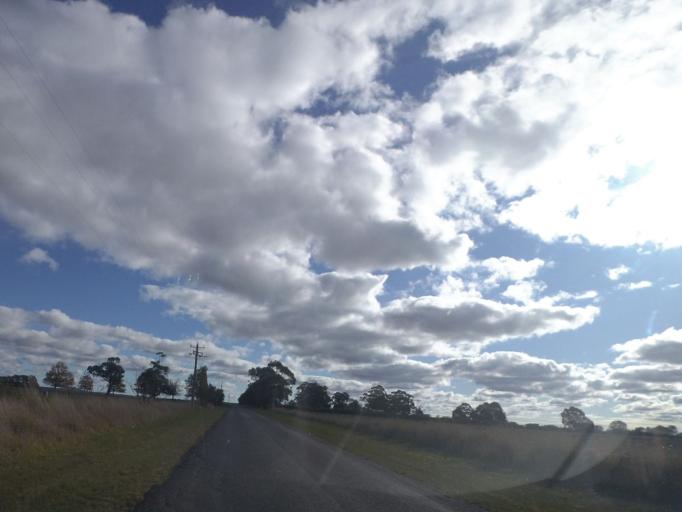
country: AU
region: Victoria
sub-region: Mount Alexander
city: Castlemaine
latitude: -37.2515
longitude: 144.4033
